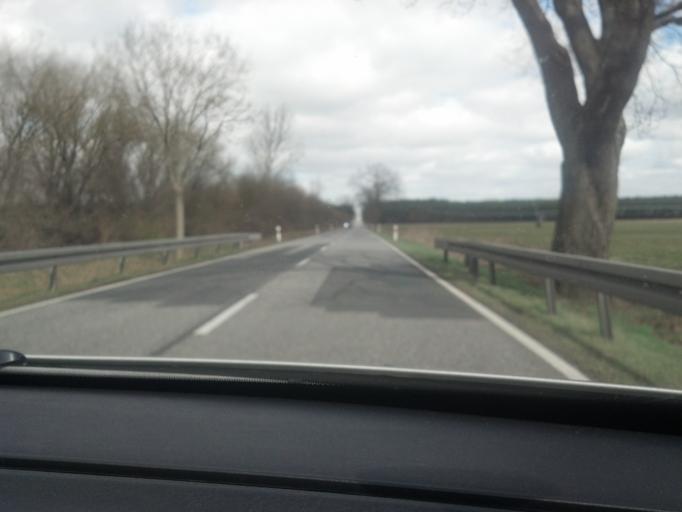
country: DE
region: Mecklenburg-Vorpommern
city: Plau am See
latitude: 53.3558
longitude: 12.2469
